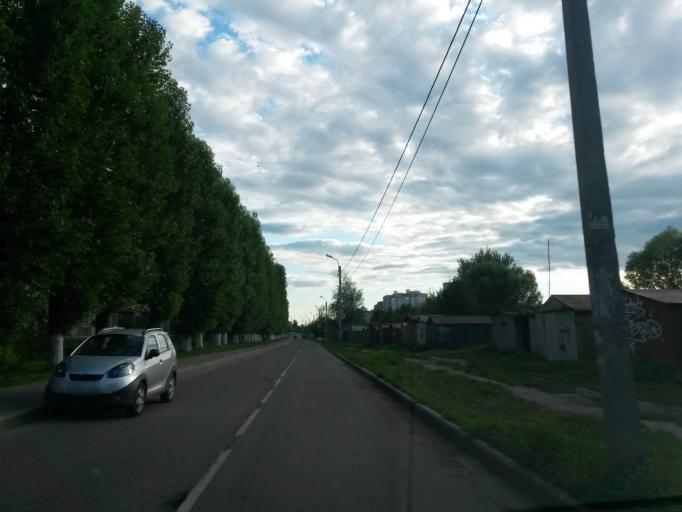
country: RU
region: Jaroslavl
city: Yaroslavl
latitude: 57.6865
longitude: 39.7733
